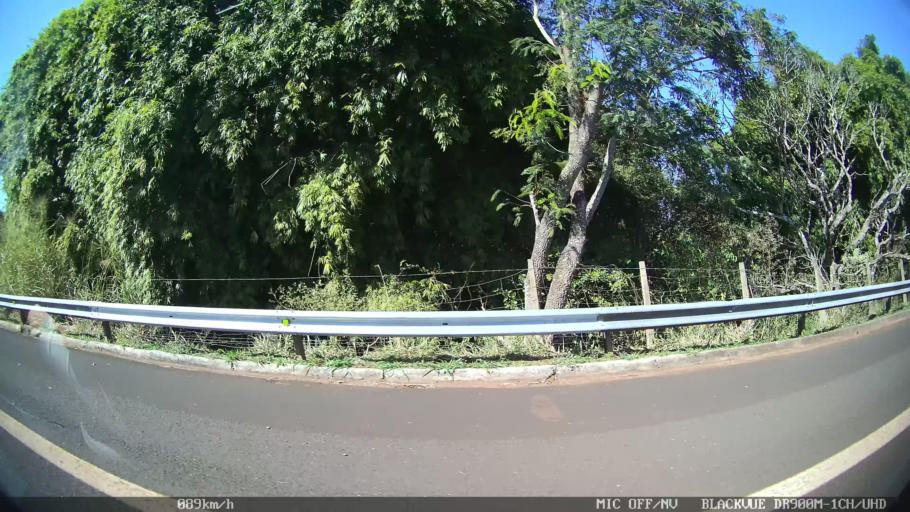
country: BR
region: Sao Paulo
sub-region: Batatais
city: Batatais
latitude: -20.7296
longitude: -47.5217
